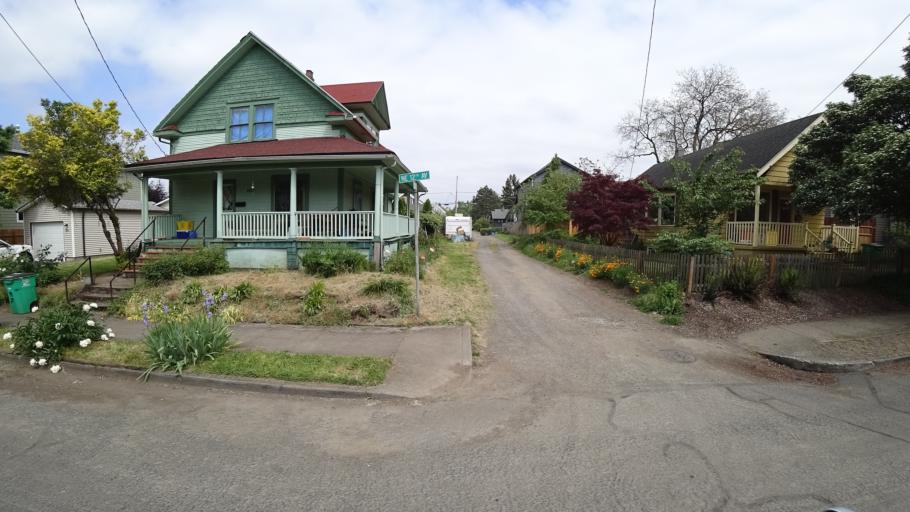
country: US
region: Oregon
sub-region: Multnomah County
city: Portland
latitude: 45.5582
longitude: -122.6537
